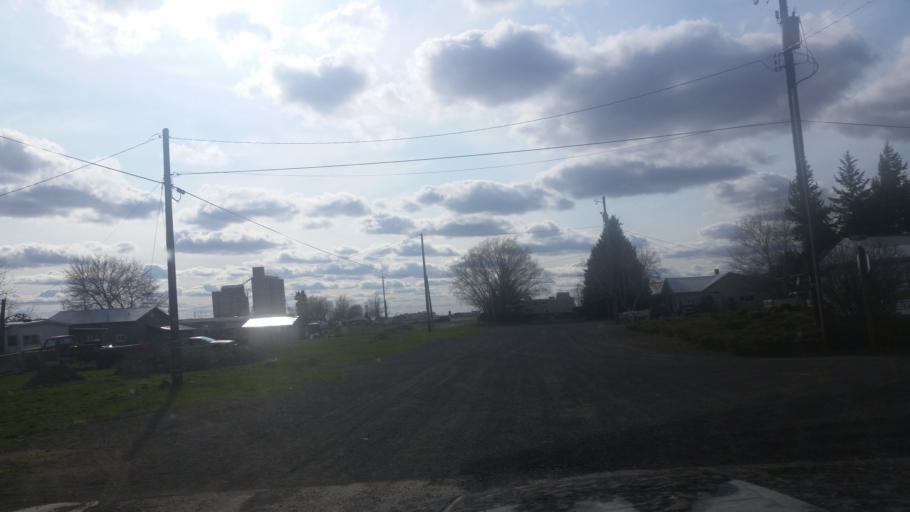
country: US
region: Washington
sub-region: Lincoln County
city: Davenport
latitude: 47.7603
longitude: -118.5201
